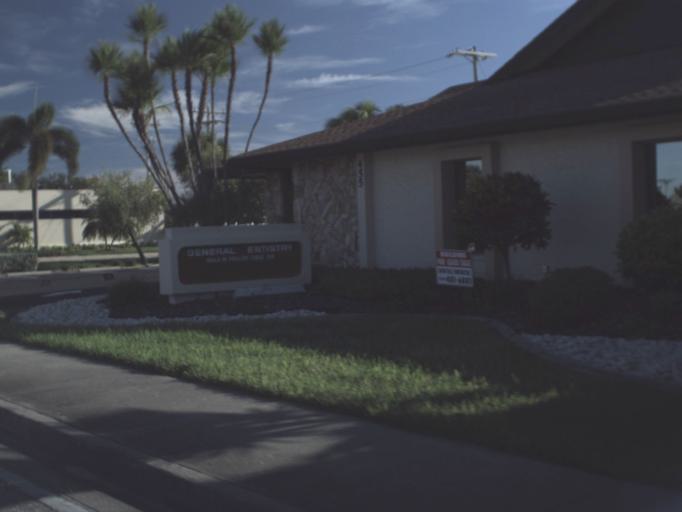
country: US
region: Florida
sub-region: Lee County
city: Lochmoor Waterway Estates
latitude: 26.6437
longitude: -81.9408
